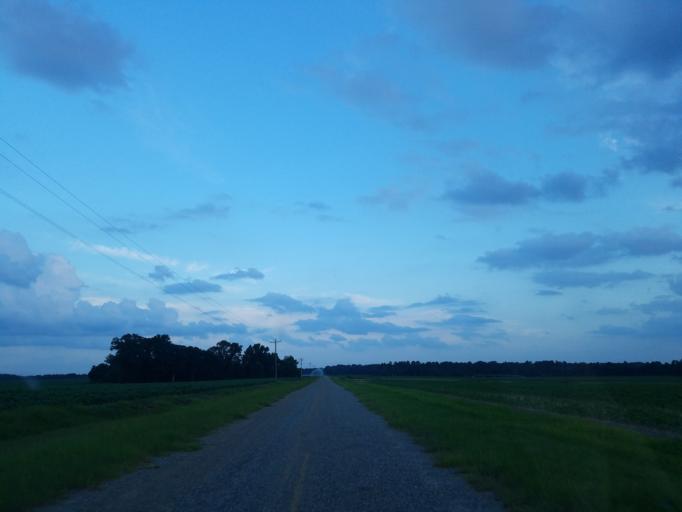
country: US
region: Georgia
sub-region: Dooly County
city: Vienna
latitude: 32.1619
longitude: -83.7317
